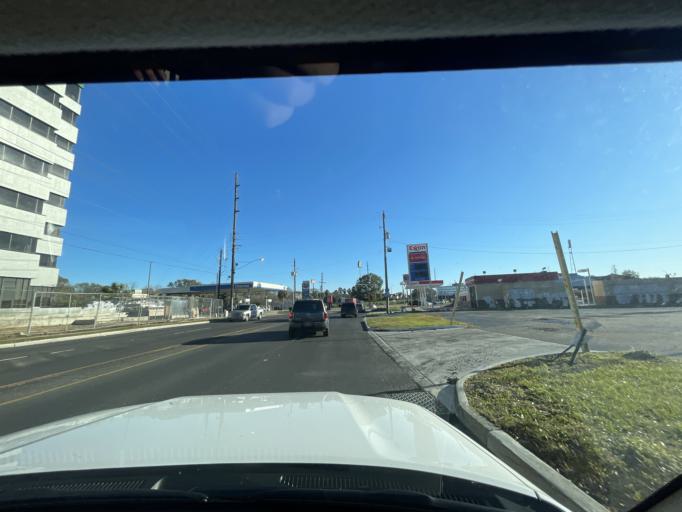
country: US
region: Louisiana
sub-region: East Baton Rouge Parish
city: Baton Rouge
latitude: 30.4267
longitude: -91.1510
